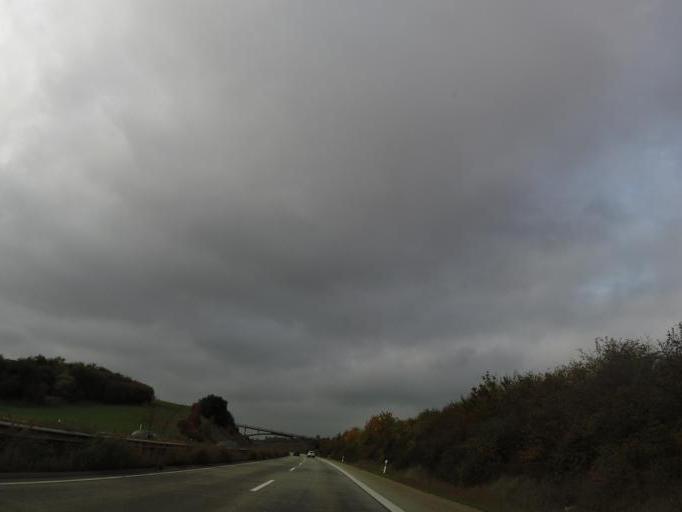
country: DE
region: Rheinland-Pfalz
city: Borrstadt
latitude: 49.5915
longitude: 7.9542
